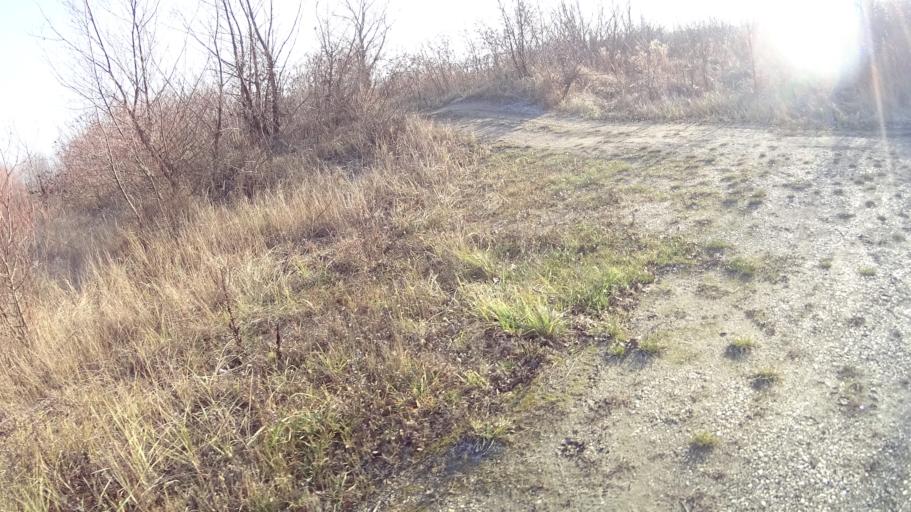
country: HU
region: Borsod-Abauj-Zemplen
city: Nyekladhaza
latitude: 47.9875
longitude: 20.8705
